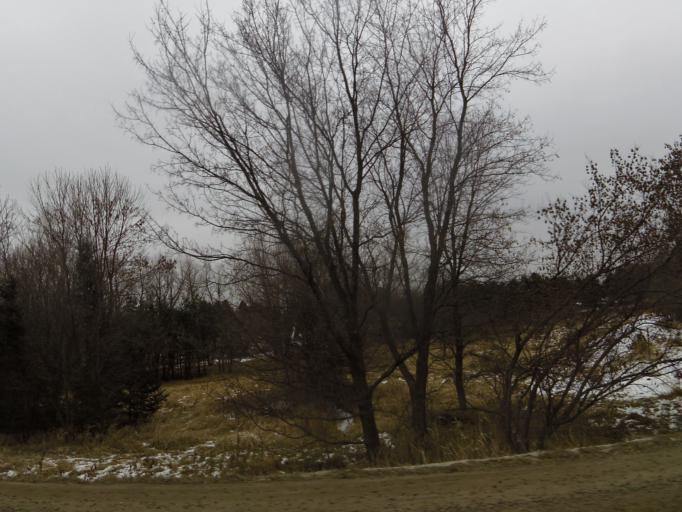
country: US
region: Minnesota
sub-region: Wright County
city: Montrose
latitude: 45.0292
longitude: -93.8583
